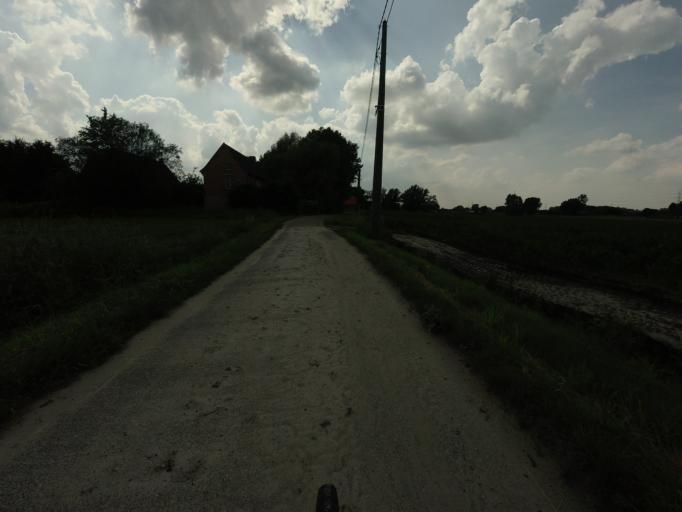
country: BE
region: Flanders
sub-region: Provincie Antwerpen
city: Duffel
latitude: 51.1144
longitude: 4.5298
